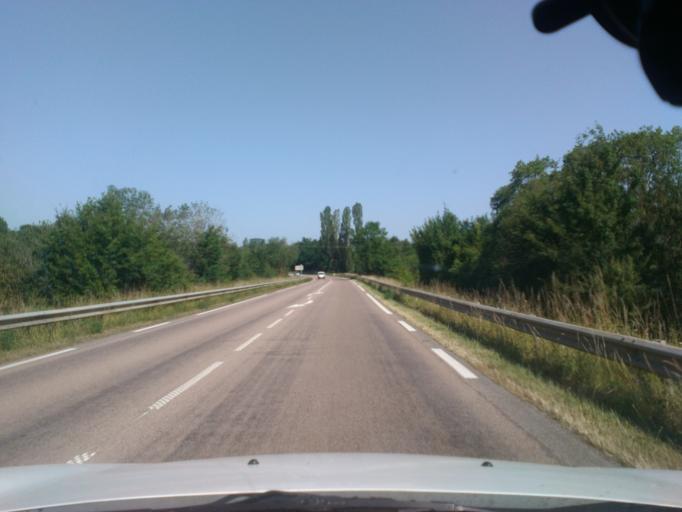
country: FR
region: Lorraine
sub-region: Departement des Vosges
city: Mirecourt
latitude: 48.3090
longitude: 6.0286
